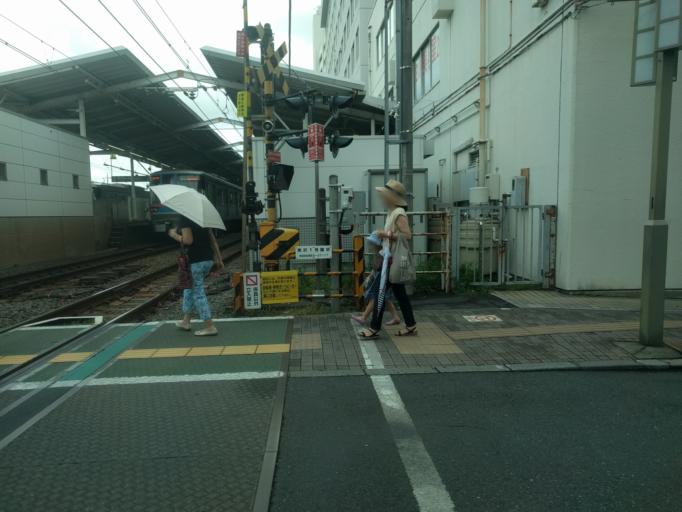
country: JP
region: Tokyo
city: Tokyo
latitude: 35.6037
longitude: 139.6720
